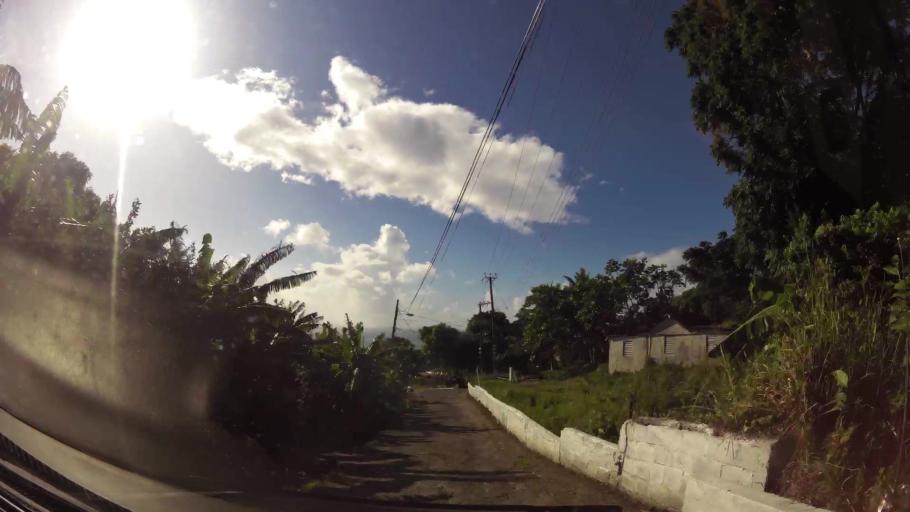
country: MS
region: Saint Peter
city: Saint Peters
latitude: 16.7499
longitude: -62.2163
